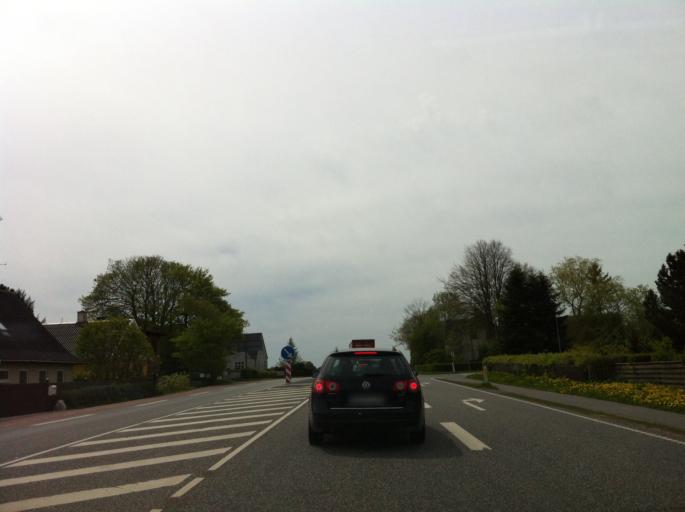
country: DK
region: Zealand
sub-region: Lejre Kommune
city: Kirke Hvalso
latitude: 55.5078
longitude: 11.8876
